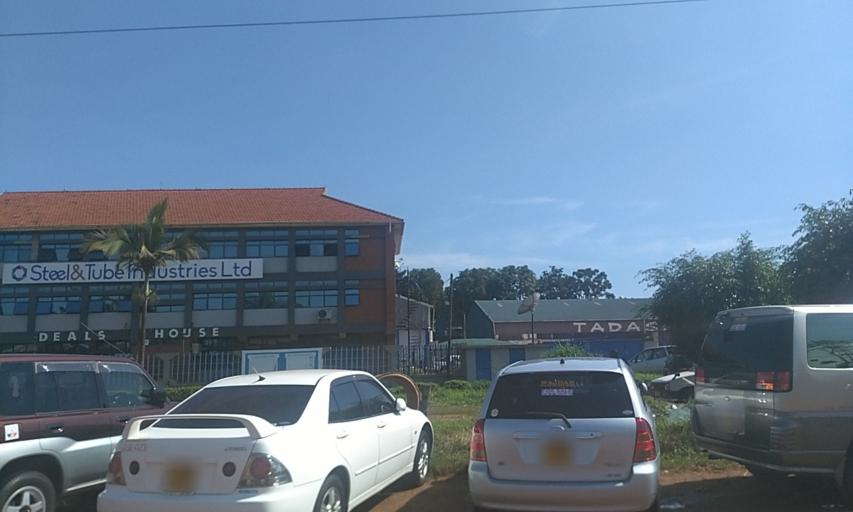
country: UG
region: Central Region
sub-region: Wakiso District
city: Kireka
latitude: 0.3375
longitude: 32.6234
